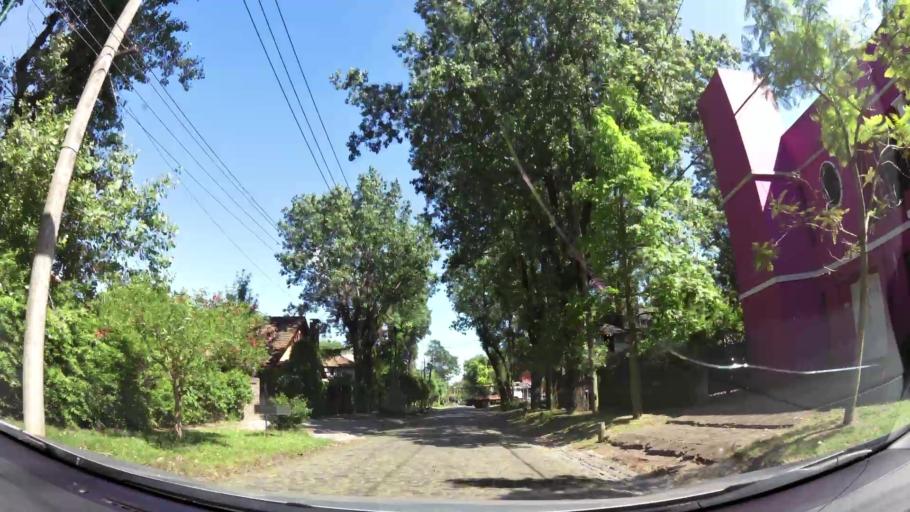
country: AR
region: Buenos Aires
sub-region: Partido de San Isidro
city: San Isidro
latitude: -34.4924
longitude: -58.5691
